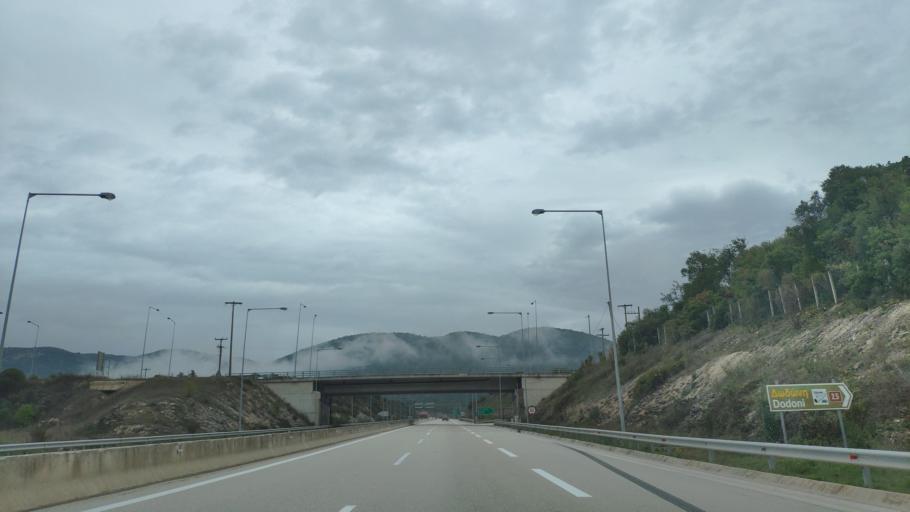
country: GR
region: Epirus
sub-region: Nomos Ioanninon
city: Pedini
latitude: 39.5600
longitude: 20.7747
